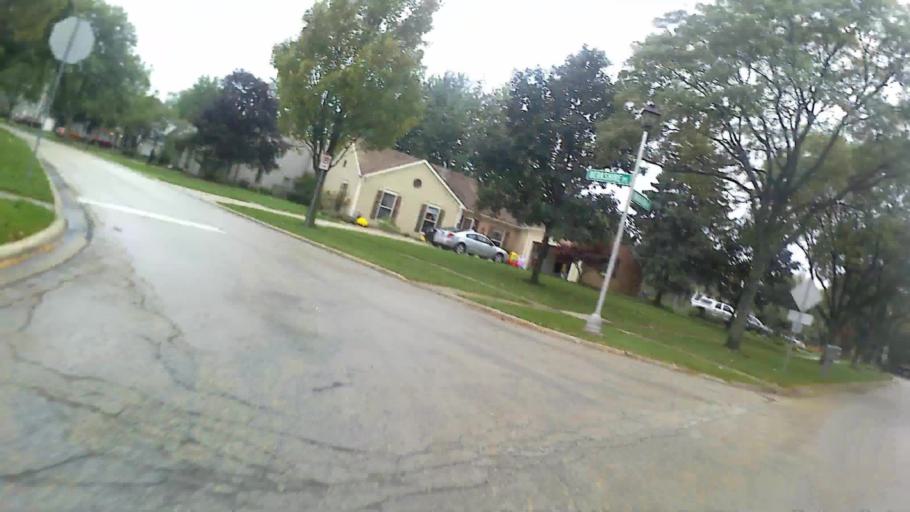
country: US
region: Illinois
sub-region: DuPage County
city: Wheaton
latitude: 41.8352
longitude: -88.1238
